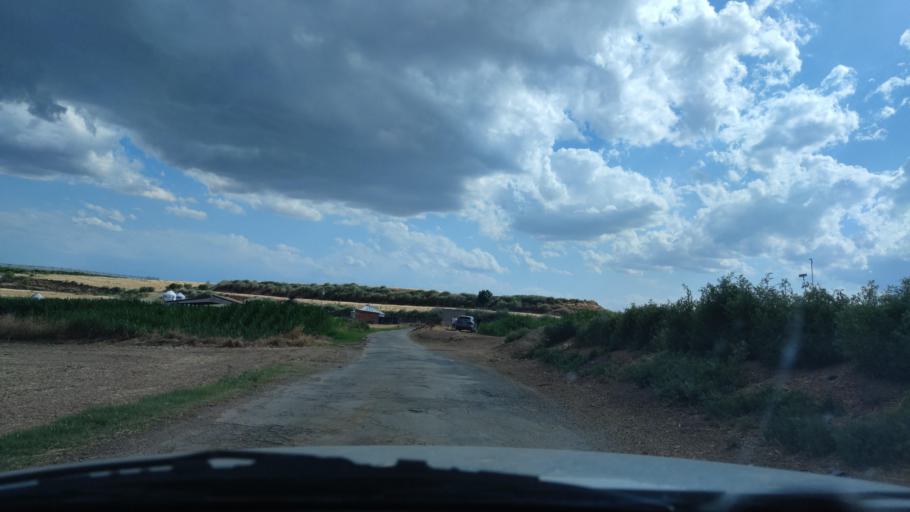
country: ES
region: Catalonia
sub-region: Provincia de Lleida
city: Alcarras
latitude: 41.5921
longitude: 0.5416
